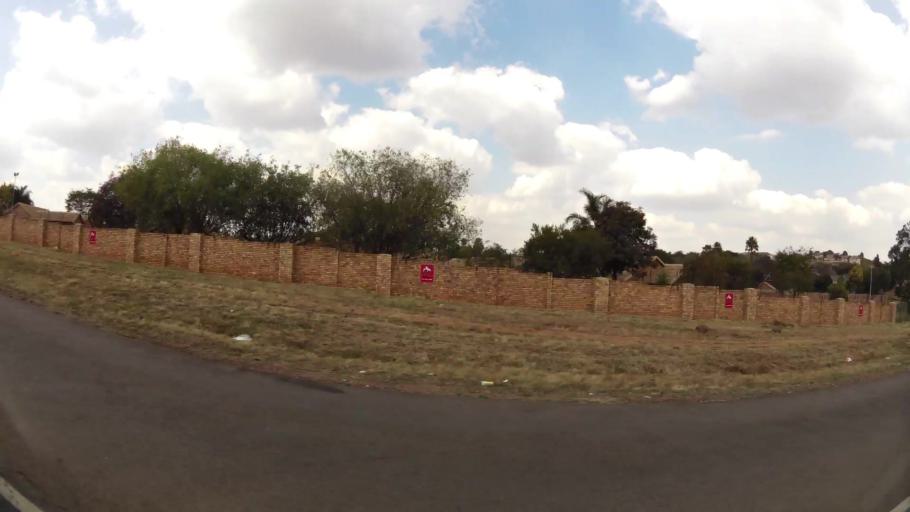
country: ZA
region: Gauteng
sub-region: City of Tshwane Metropolitan Municipality
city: Centurion
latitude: -25.8334
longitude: 28.2536
